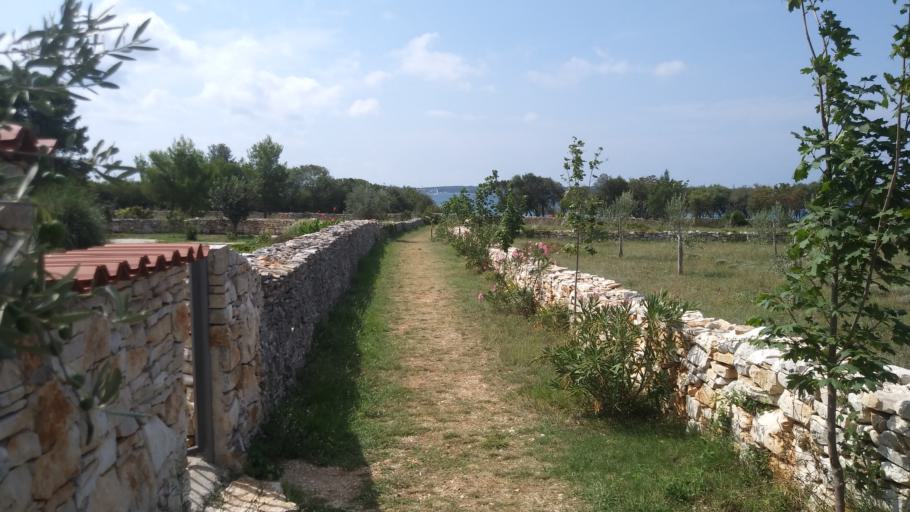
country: HR
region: Istarska
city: Fazana
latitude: 44.9484
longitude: 13.7875
